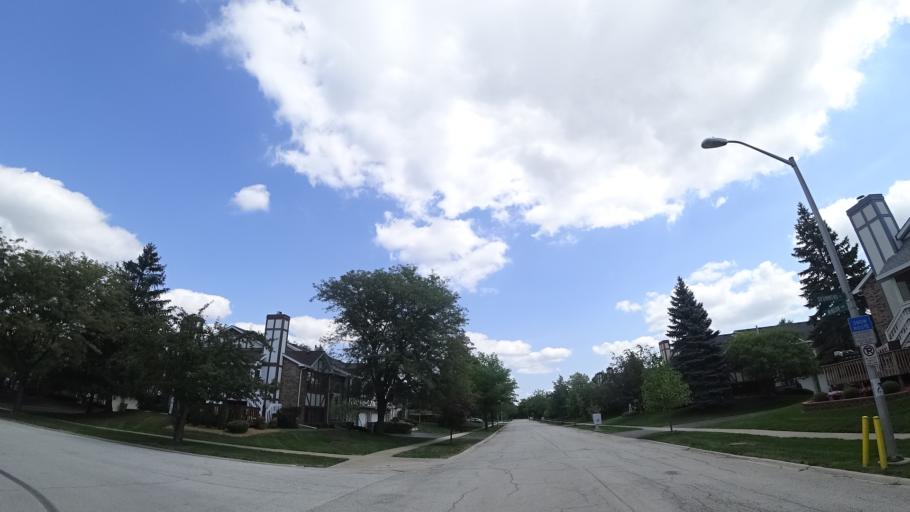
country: US
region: Illinois
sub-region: Cook County
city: Orland Hills
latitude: 41.5701
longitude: -87.8464
